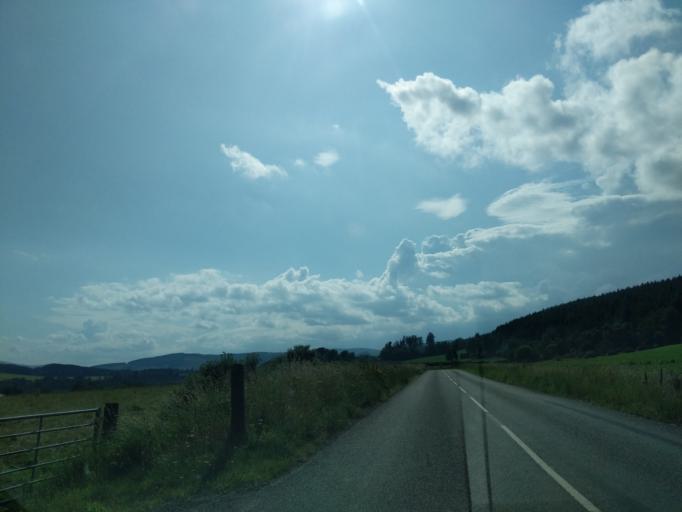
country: GB
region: Scotland
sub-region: Moray
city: Rothes
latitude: 57.5471
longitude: -3.1671
